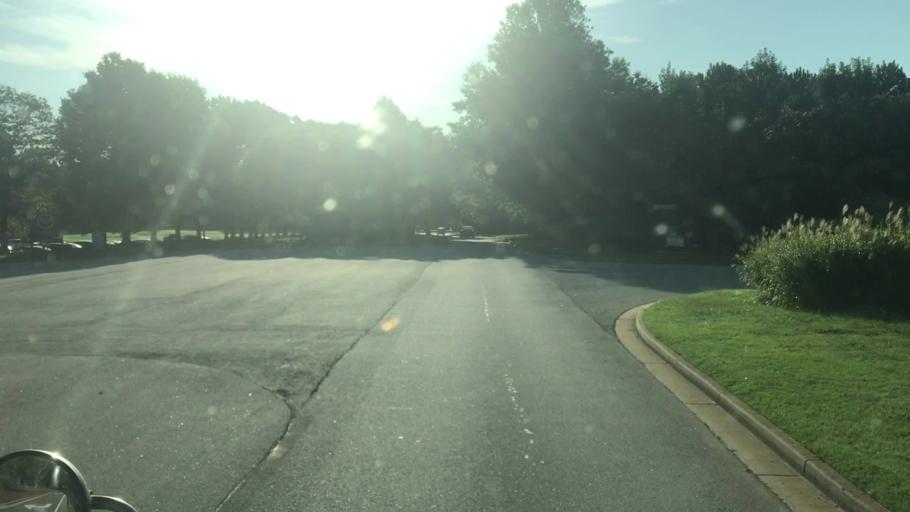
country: US
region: Georgia
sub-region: Henry County
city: McDonough
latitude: 33.3900
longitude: -84.1719
